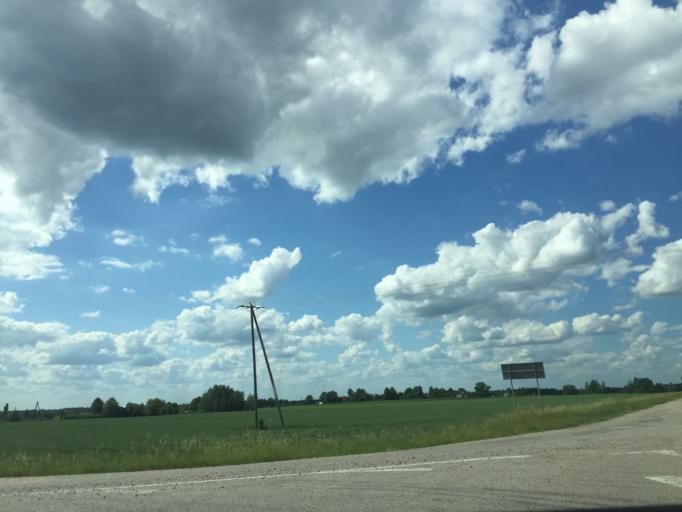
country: LV
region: Tukuma Rajons
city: Tukums
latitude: 56.9197
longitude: 23.2111
